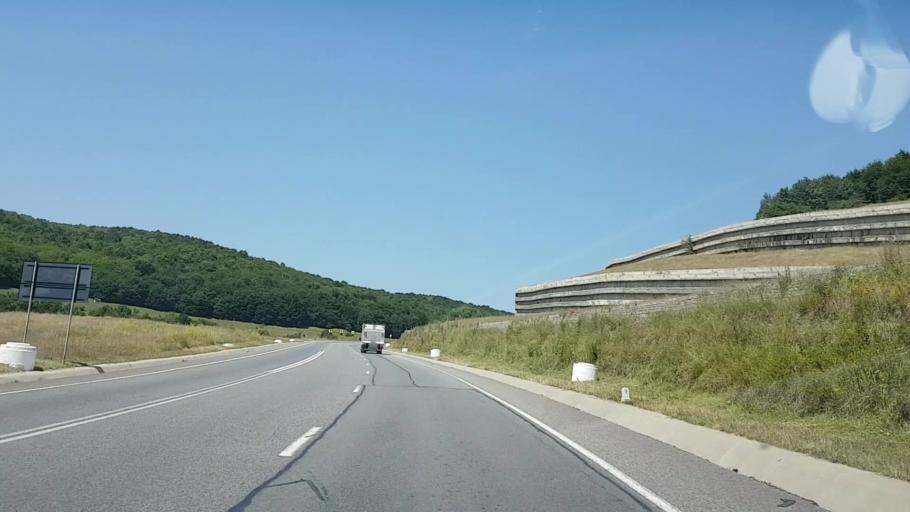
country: RO
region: Cluj
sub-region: Comuna Feleacu
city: Feleacu
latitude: 46.6927
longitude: 23.6368
